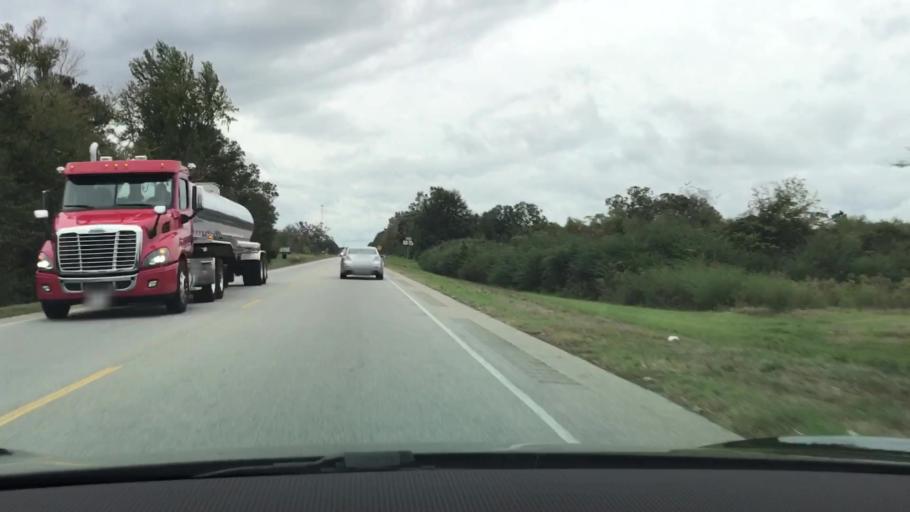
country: US
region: Georgia
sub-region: Jefferson County
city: Wadley
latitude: 32.9264
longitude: -82.3973
